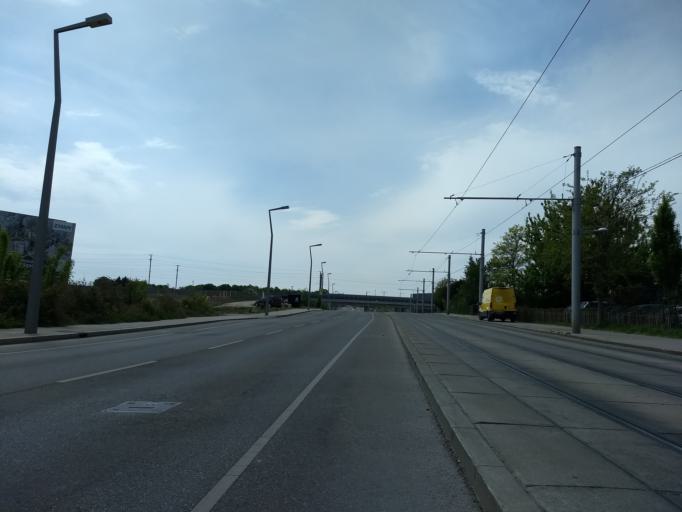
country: AT
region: Lower Austria
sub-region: Politischer Bezirk Wien-Umgebung
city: Gerasdorf bei Wien
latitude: 48.2356
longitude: 16.4882
